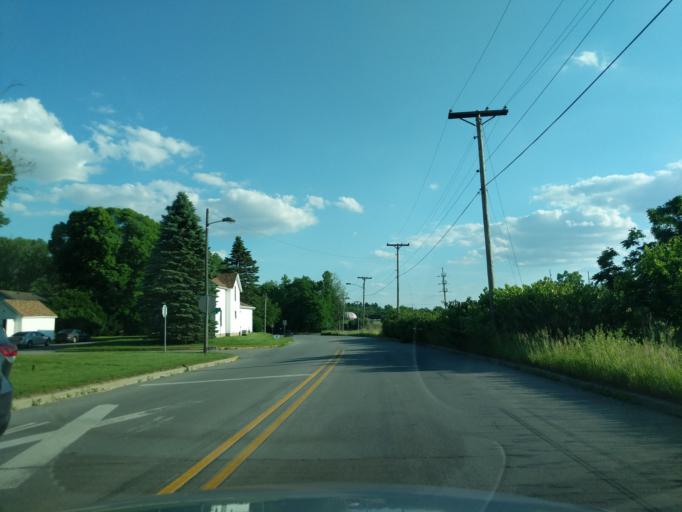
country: US
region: Indiana
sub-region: Whitley County
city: Columbia City
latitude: 41.1486
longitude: -85.4880
